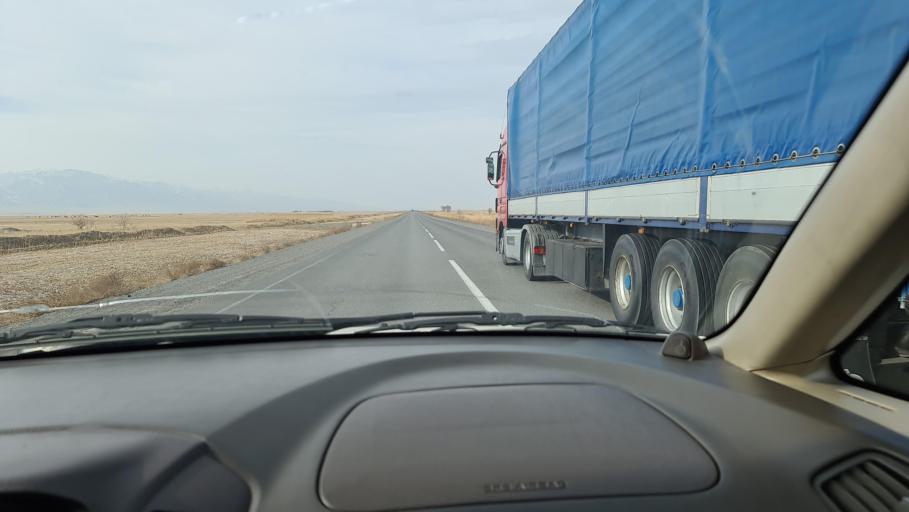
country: KG
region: Chuy
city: Bystrovka
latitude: 43.3314
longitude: 75.6386
